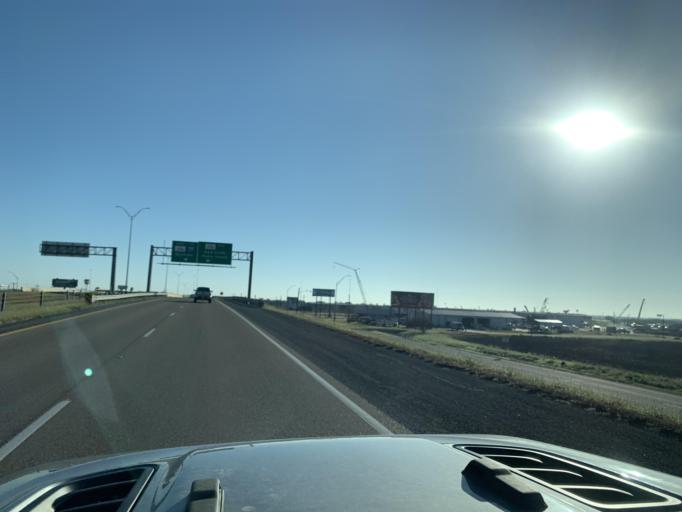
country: US
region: Texas
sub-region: Nueces County
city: Corpus Christi
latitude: 27.7817
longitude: -97.4793
